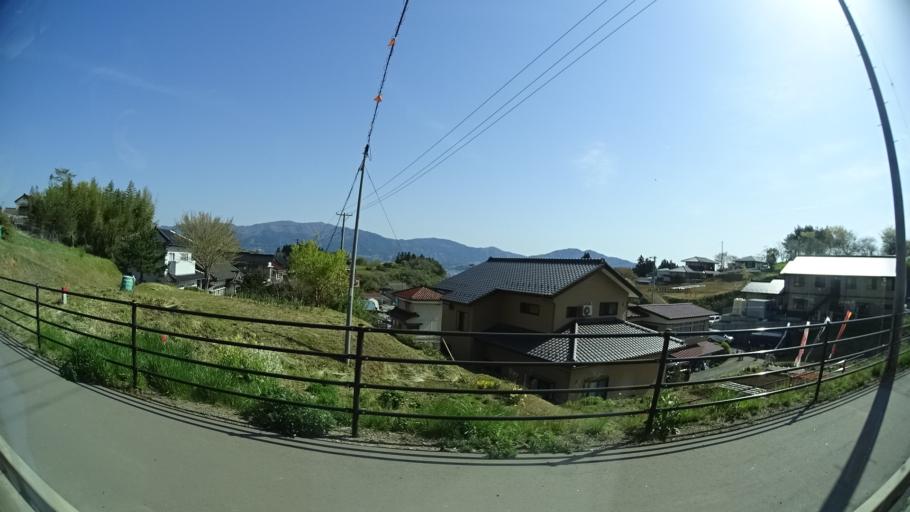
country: JP
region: Iwate
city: Ofunato
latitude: 38.9797
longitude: 141.6225
